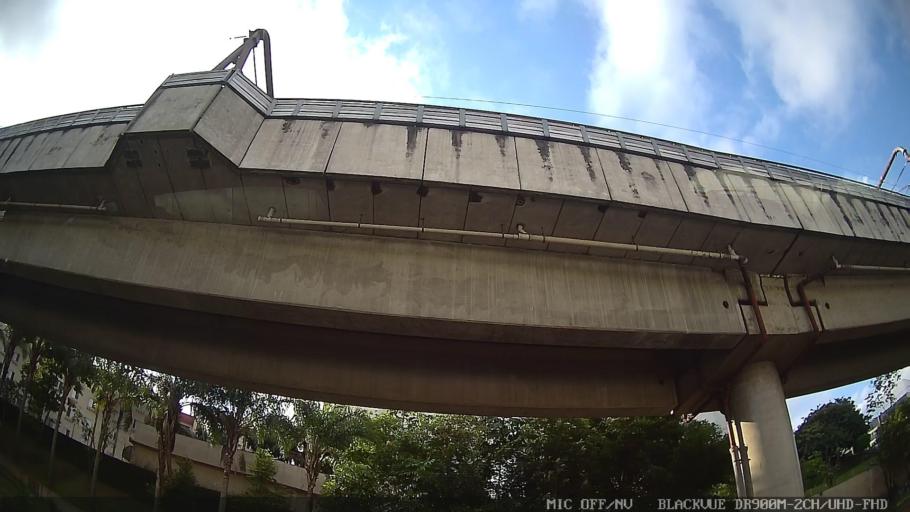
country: BR
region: Sao Paulo
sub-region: Taboao Da Serra
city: Taboao da Serra
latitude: -23.6473
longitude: -46.7578
